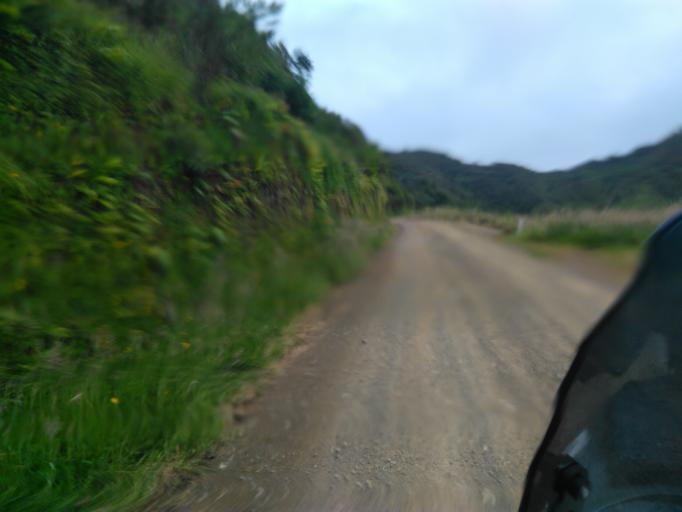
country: NZ
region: Bay of Plenty
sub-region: Opotiki District
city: Opotiki
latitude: -38.0967
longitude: 177.4856
